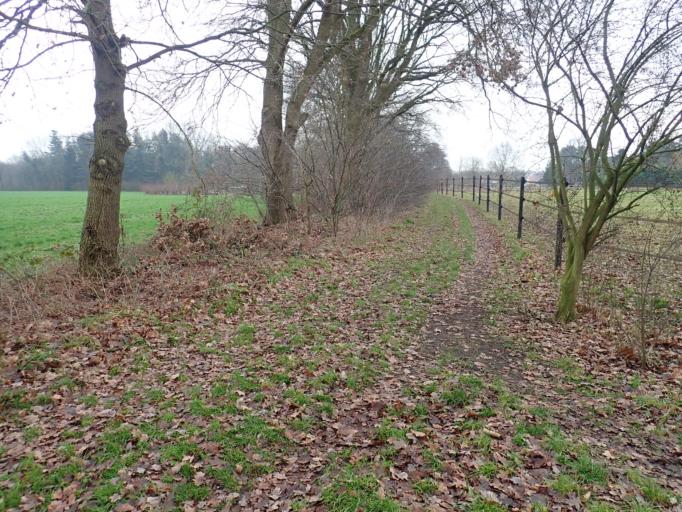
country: BE
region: Flanders
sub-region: Provincie Antwerpen
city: Schilde
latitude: 51.2151
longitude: 4.6098
